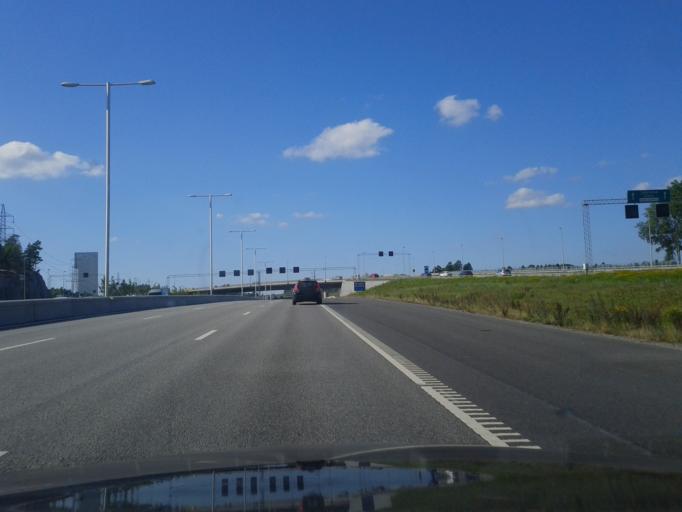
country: SE
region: Stockholm
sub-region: Stockholms Kommun
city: Kista
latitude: 59.3996
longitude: 17.9767
